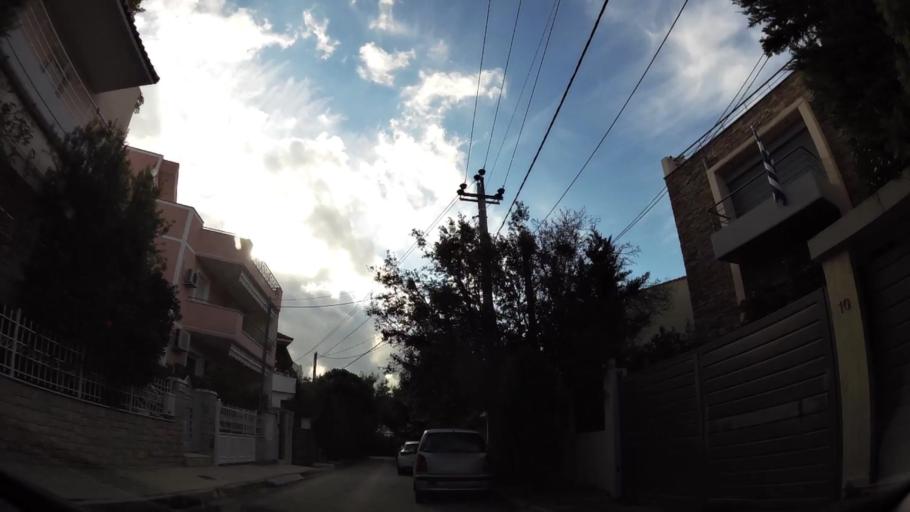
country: GR
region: Attica
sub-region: Nomarchia Athinas
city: Vrilissia
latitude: 38.0404
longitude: 23.8236
